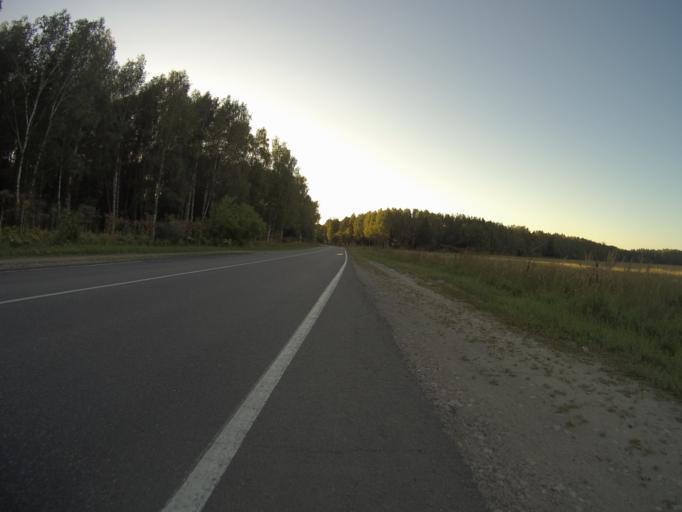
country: RU
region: Vladimir
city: Anopino
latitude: 55.7351
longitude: 40.7219
